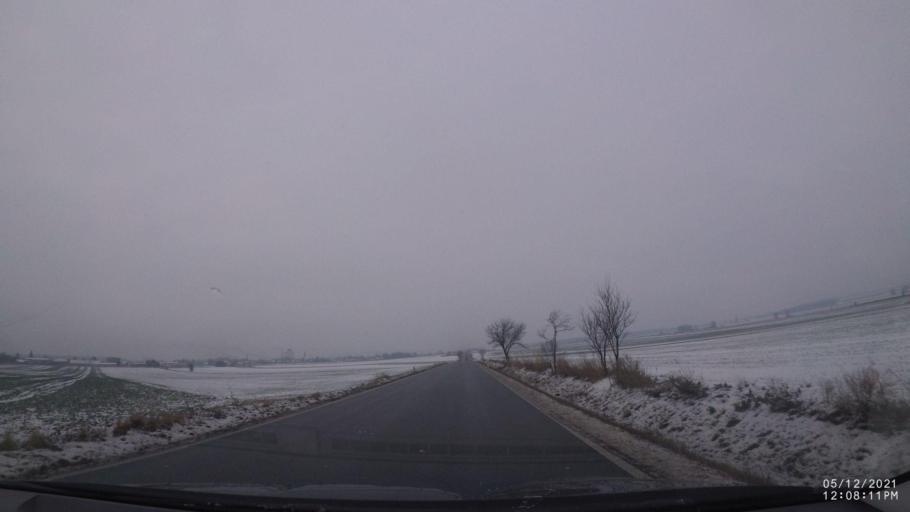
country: CZ
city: Ceske Mezirici
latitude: 50.2920
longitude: 16.0244
